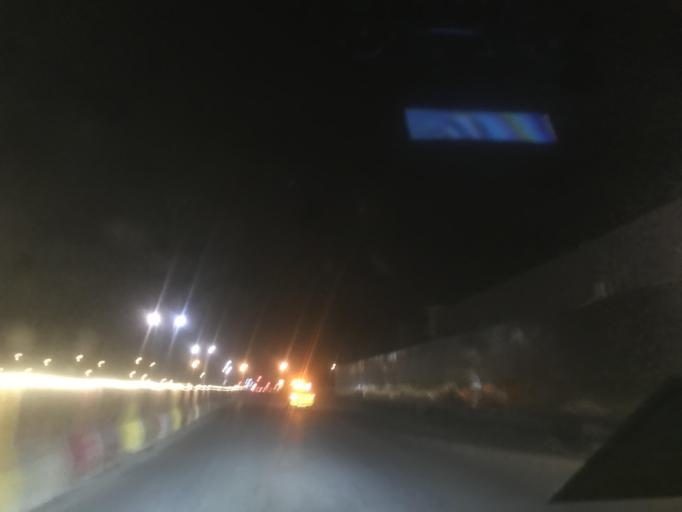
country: SA
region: Ar Riyad
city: Riyadh
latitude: 24.7967
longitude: 46.5902
